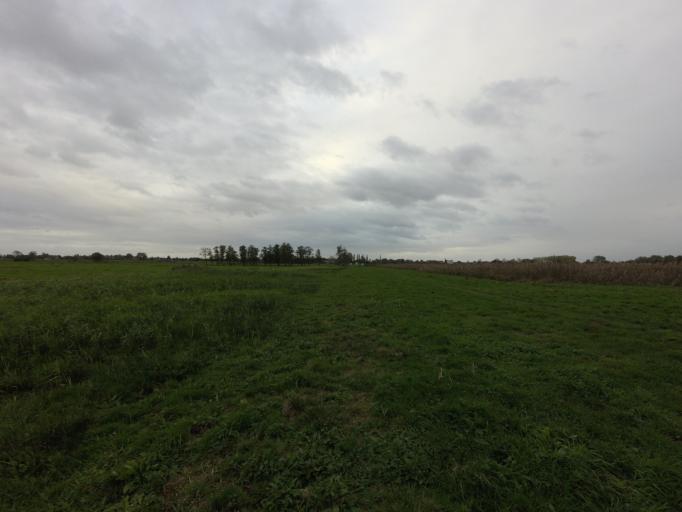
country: NL
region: Utrecht
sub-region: Gemeente De Ronde Venen
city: Mijdrecht
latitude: 52.2038
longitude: 4.9141
